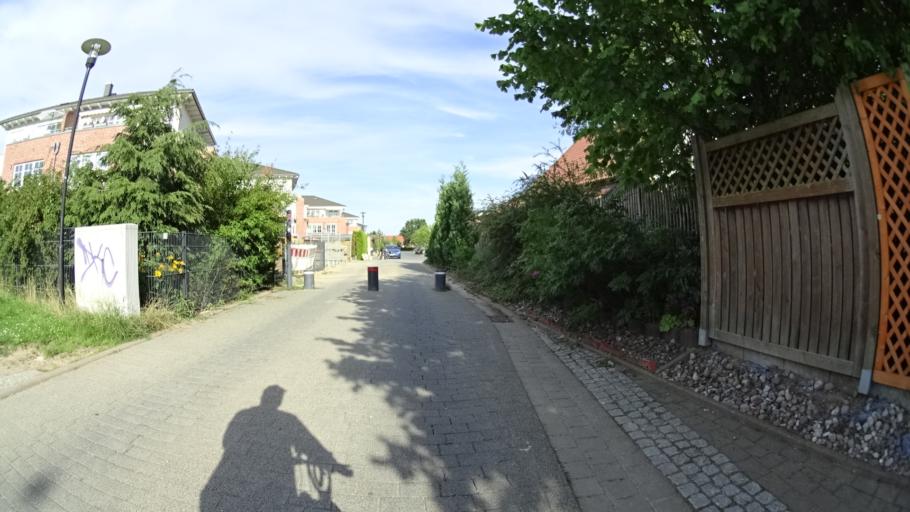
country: DE
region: Lower Saxony
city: Lueneburg
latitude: 53.2362
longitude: 10.3851
